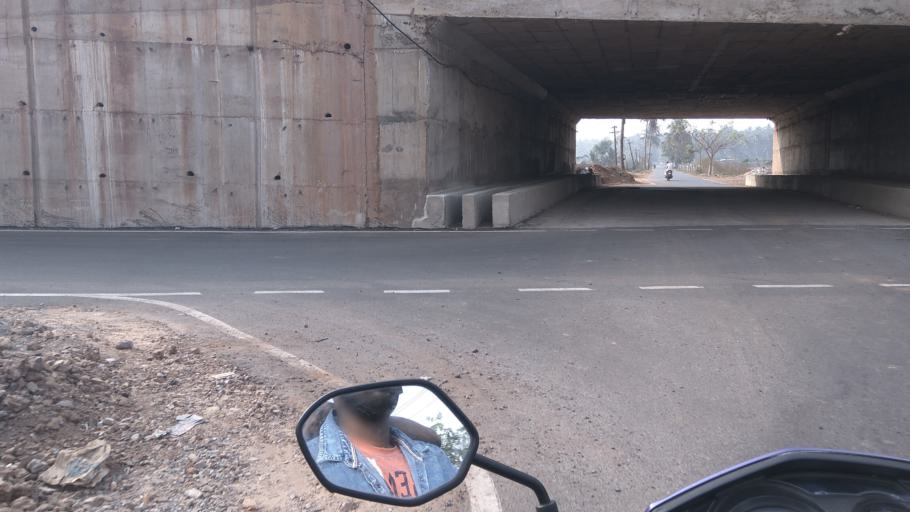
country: IN
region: Goa
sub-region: North Goa
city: Panaji
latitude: 15.4962
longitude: 73.8569
